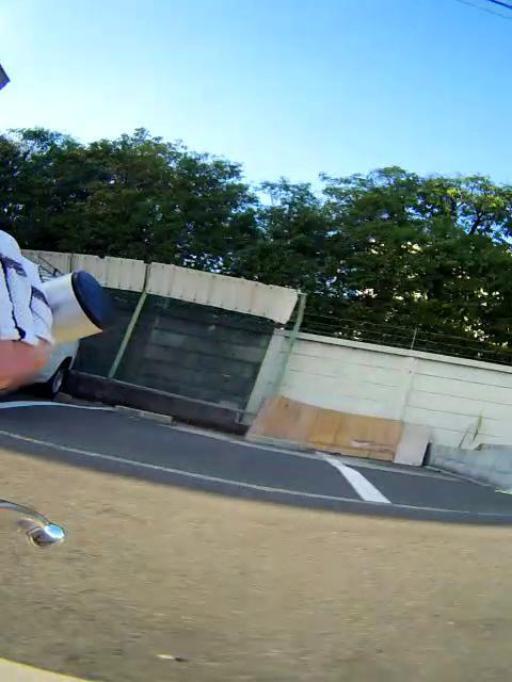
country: JP
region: Hyogo
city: Itami
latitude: 34.7815
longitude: 135.3959
